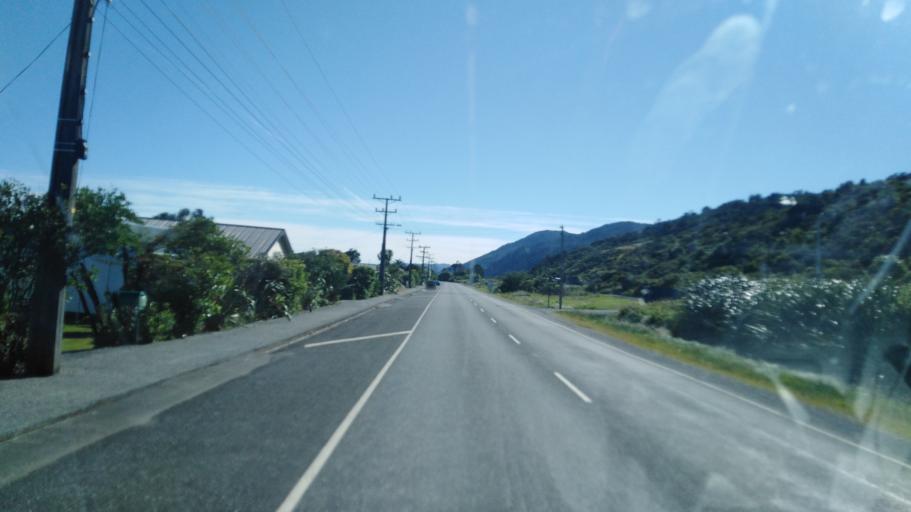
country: NZ
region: West Coast
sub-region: Buller District
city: Westport
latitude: -41.6212
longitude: 171.8617
